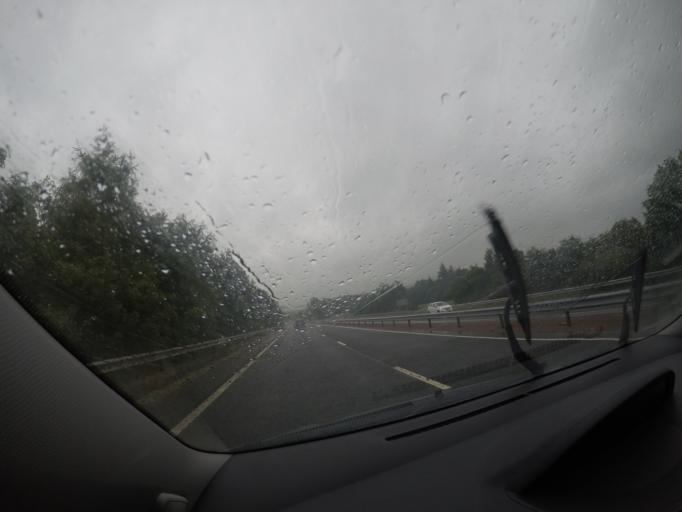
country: GB
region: Scotland
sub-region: Angus
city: Forfar
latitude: 56.6008
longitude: -2.9066
